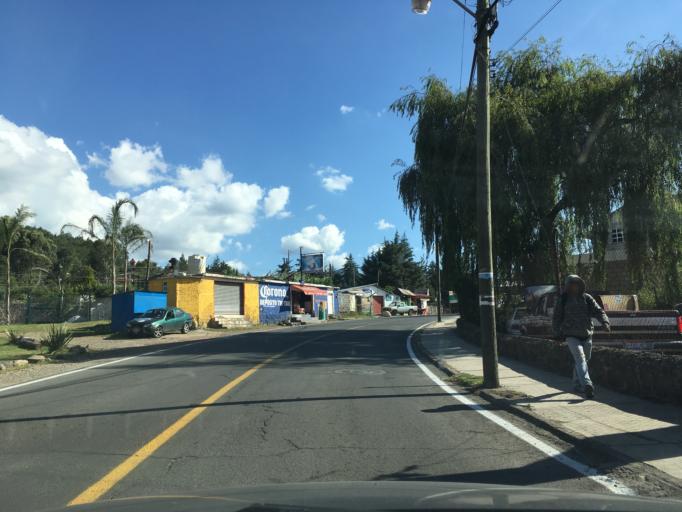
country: MX
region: Hidalgo
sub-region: Omitlan de Juarez
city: San Antonio el Paso
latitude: 20.2066
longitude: -98.5702
